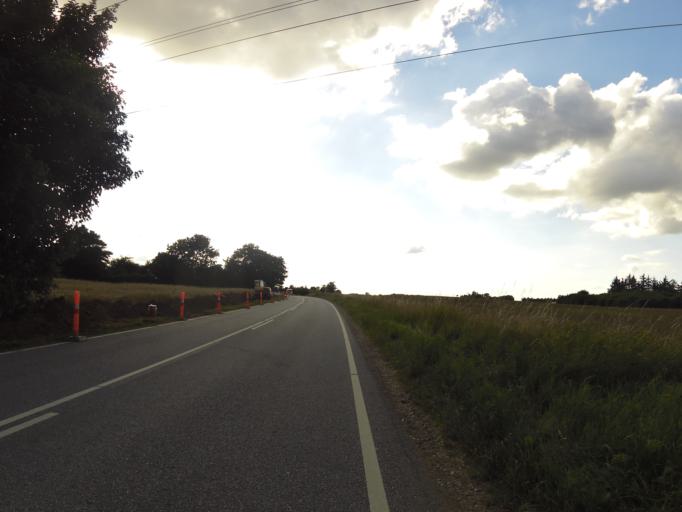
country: DK
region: South Denmark
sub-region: Haderslev Kommune
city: Vojens
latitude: 55.1975
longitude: 9.3239
